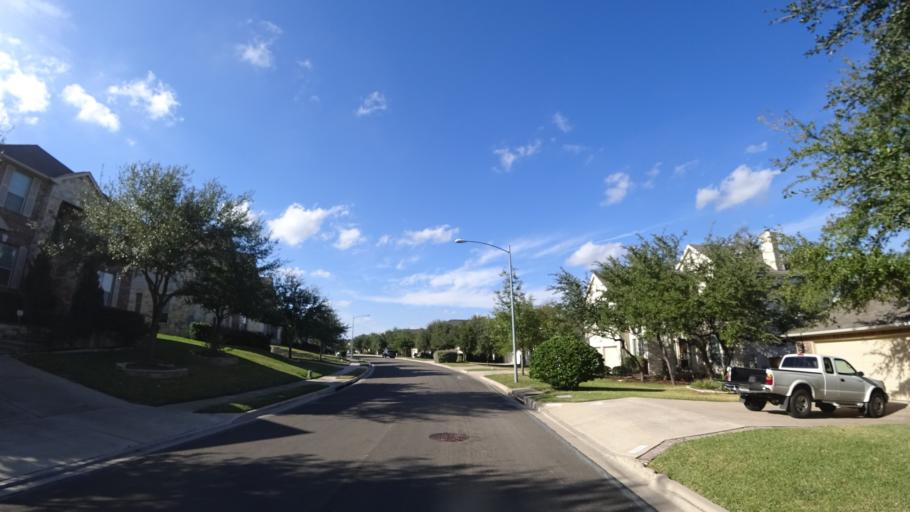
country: US
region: Texas
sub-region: Travis County
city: Barton Creek
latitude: 30.2502
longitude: -97.8732
